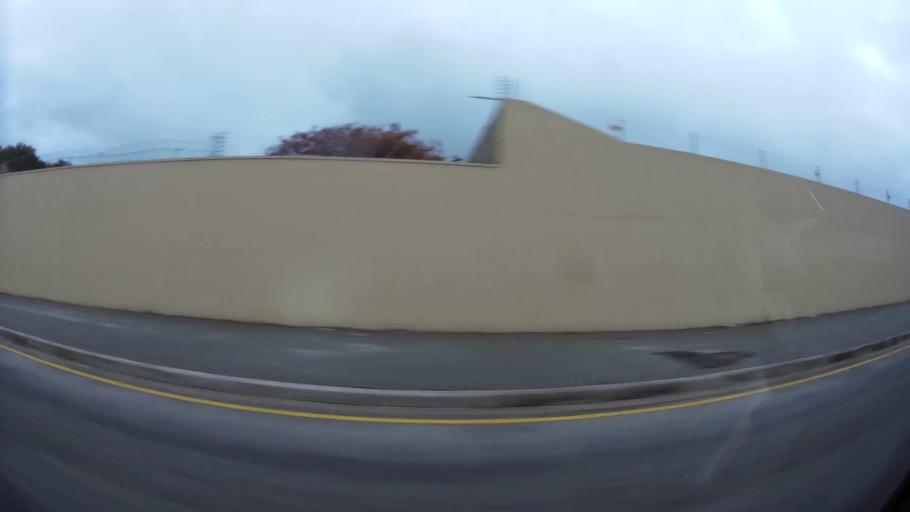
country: ZA
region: Eastern Cape
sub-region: Nelson Mandela Bay Metropolitan Municipality
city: Port Elizabeth
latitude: -33.9460
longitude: 25.6040
